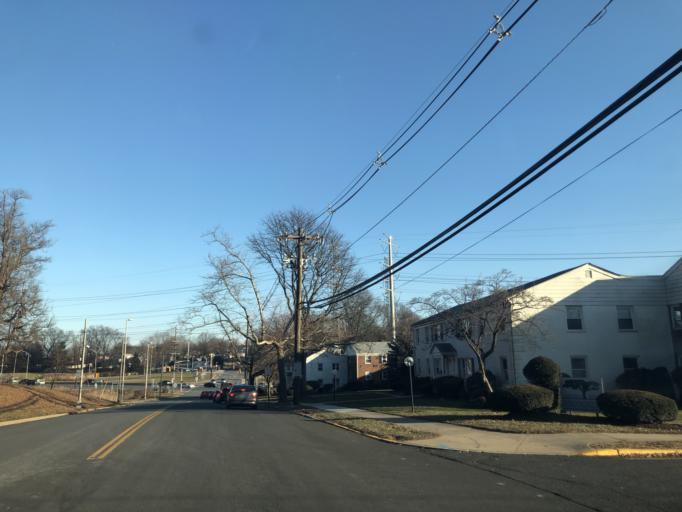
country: US
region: New Jersey
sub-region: Middlesex County
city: Metuchen
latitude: 40.5401
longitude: -74.3409
